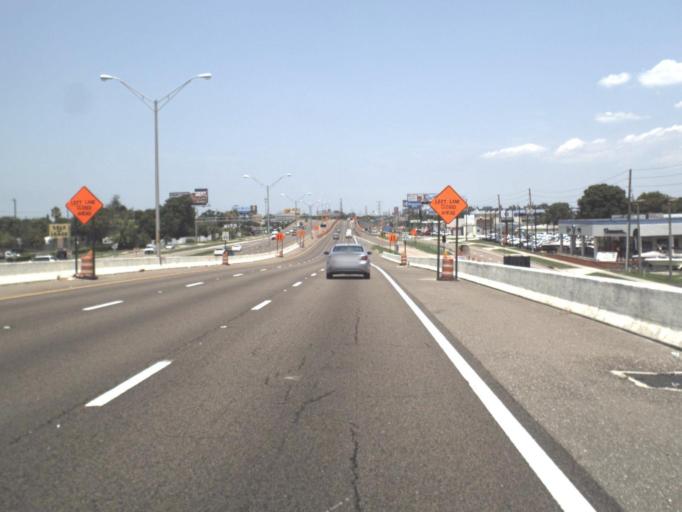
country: US
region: Florida
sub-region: Pinellas County
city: South Highpoint
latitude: 27.9176
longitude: -82.7297
